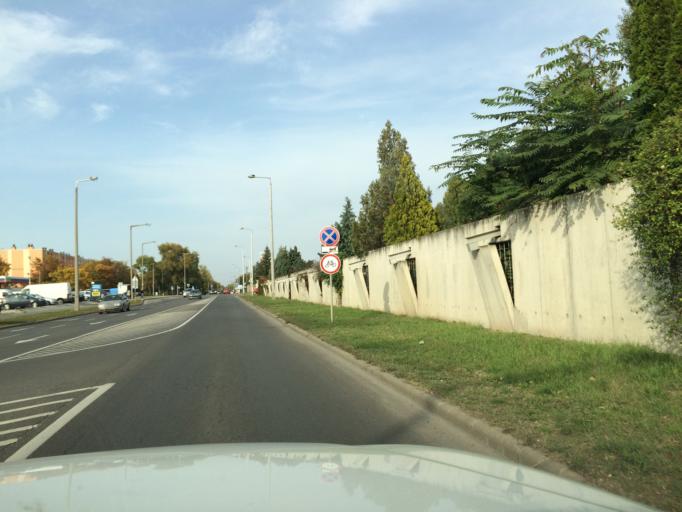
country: HU
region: Szabolcs-Szatmar-Bereg
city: Nyiregyhaza
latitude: 47.9691
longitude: 21.7251
